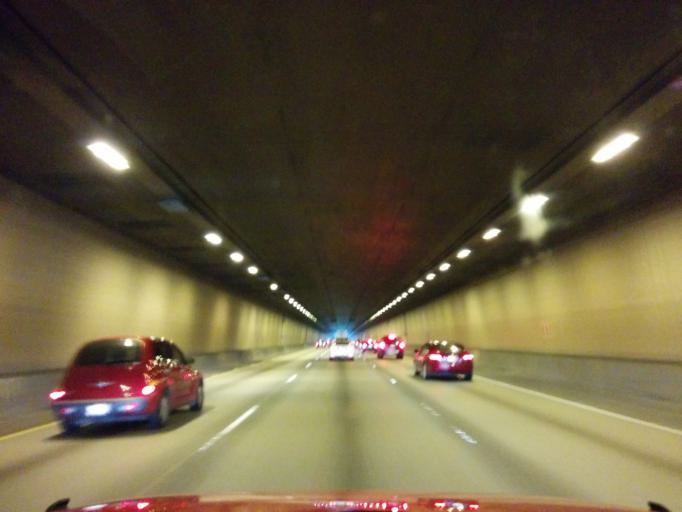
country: US
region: Washington
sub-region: King County
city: Seattle
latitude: 47.5904
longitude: -122.2890
